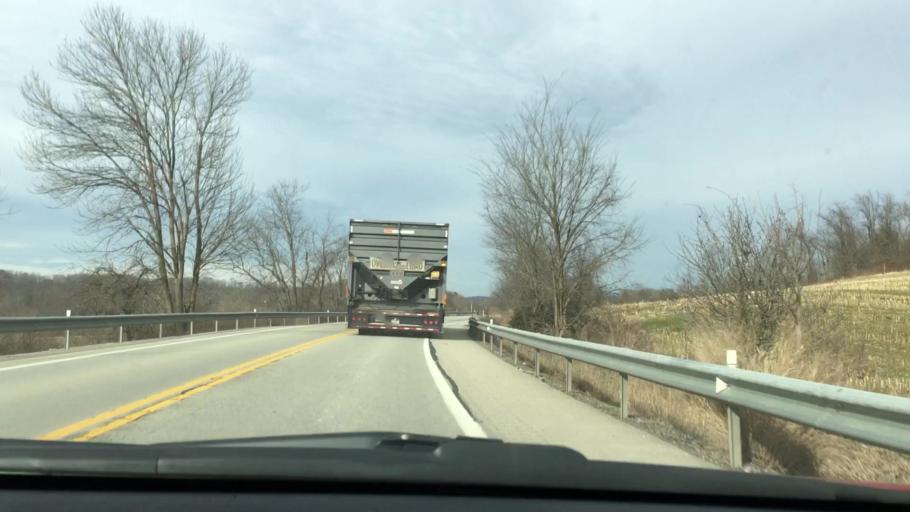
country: US
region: Pennsylvania
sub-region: Greene County
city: Fairdale
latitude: 39.8646
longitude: -79.9706
